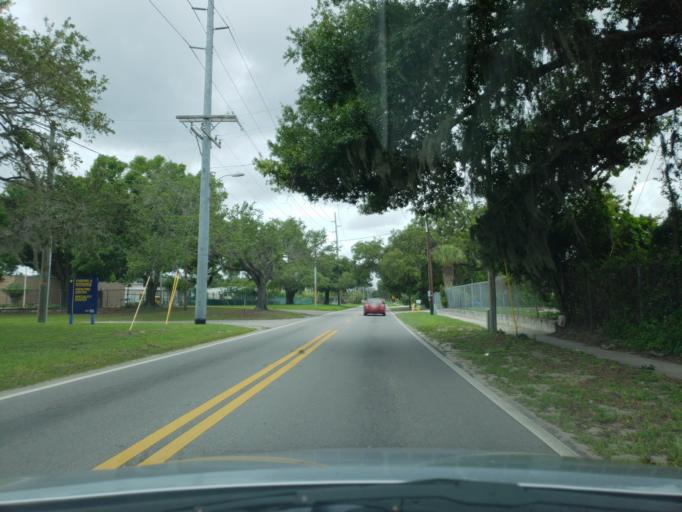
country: US
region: Florida
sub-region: Hillsborough County
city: Temple Terrace
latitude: 28.0034
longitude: -82.4274
